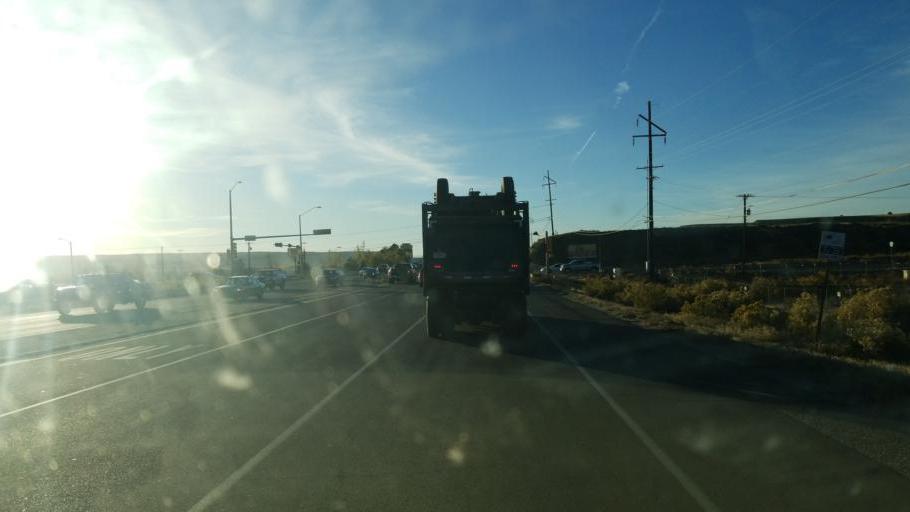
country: US
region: New Mexico
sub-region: San Juan County
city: Lee Acres
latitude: 36.7021
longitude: -108.0937
